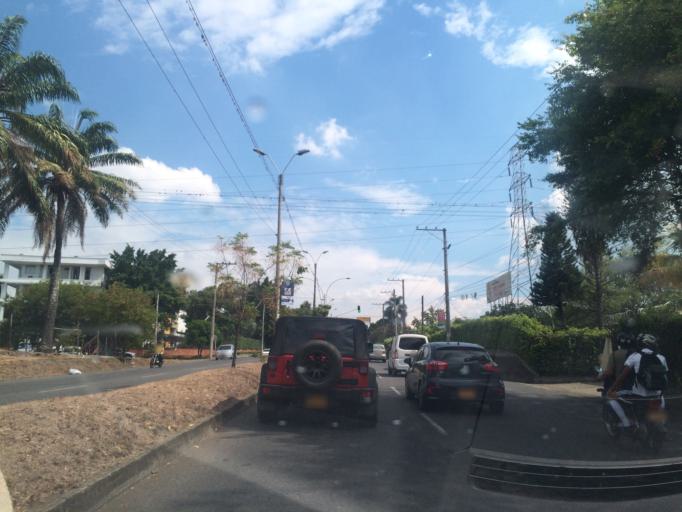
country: CO
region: Valle del Cauca
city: Cali
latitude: 3.3514
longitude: -76.5303
